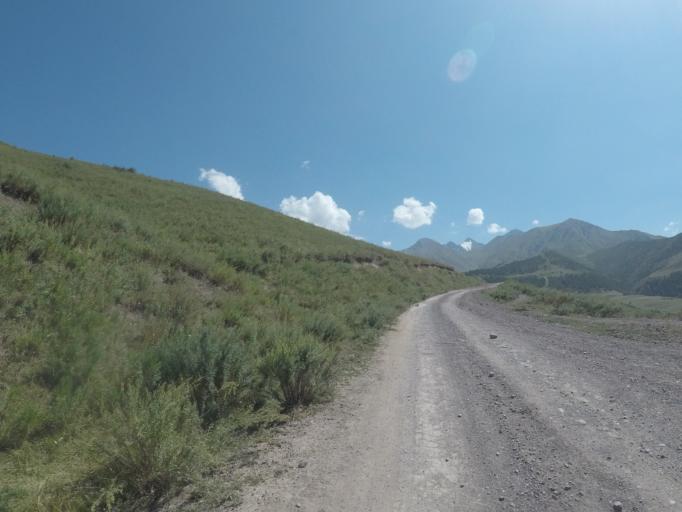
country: KG
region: Chuy
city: Bishkek
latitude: 42.6495
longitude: 74.5211
